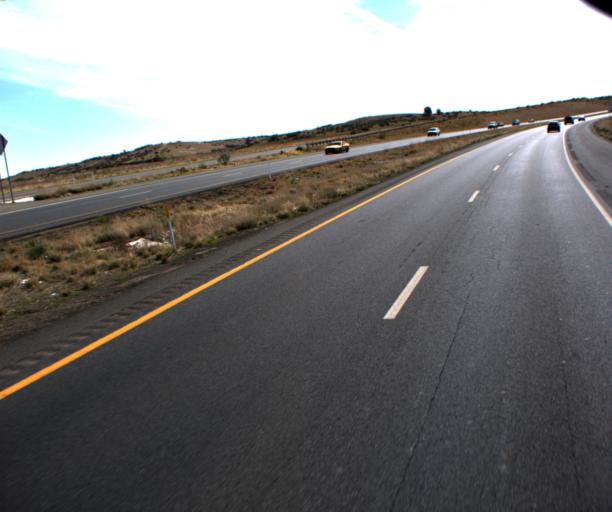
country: US
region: Arizona
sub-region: Yavapai County
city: Prescott Valley
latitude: 34.6372
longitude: -112.4042
